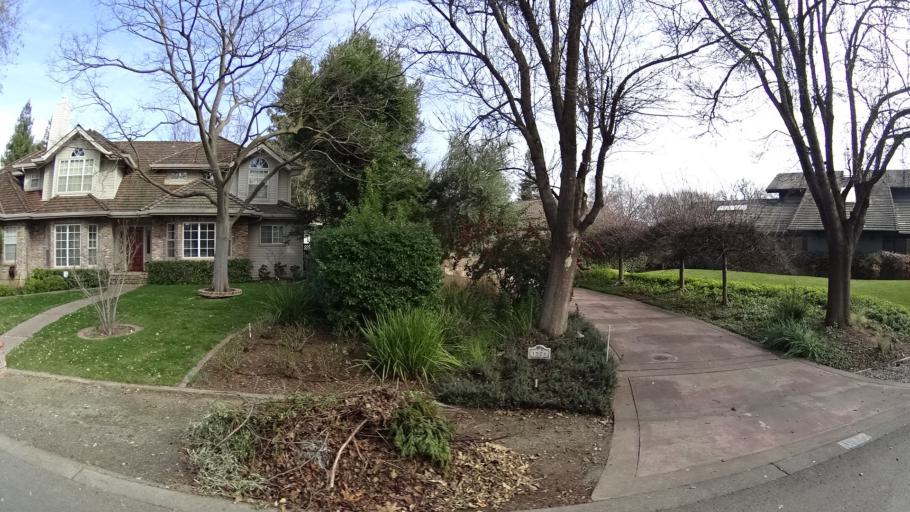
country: US
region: California
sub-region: Yolo County
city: Davis
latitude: 38.5374
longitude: -121.7171
